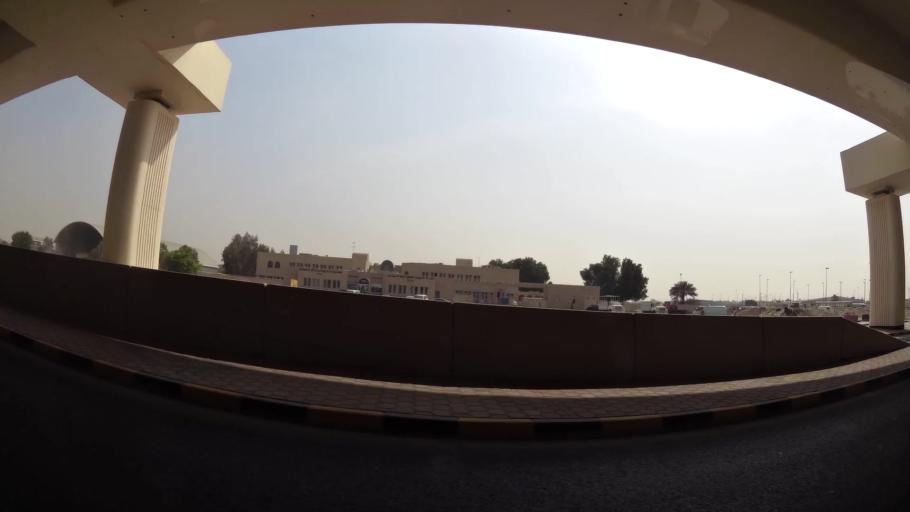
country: KW
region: Al Asimah
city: Ar Rabiyah
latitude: 29.3144
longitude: 47.8936
